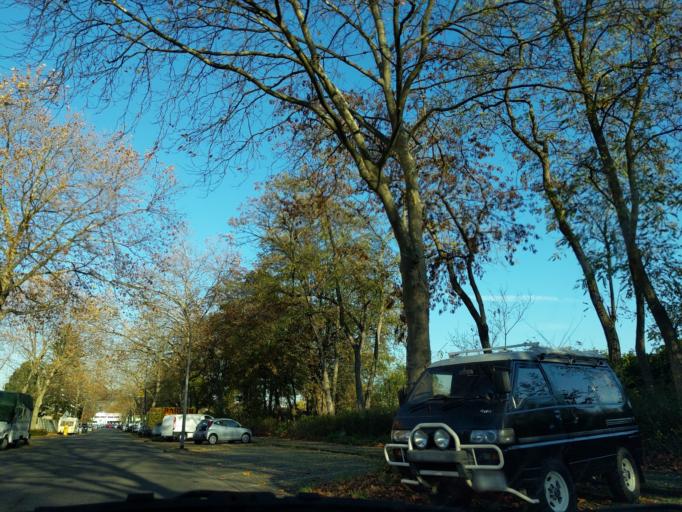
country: DE
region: North Rhine-Westphalia
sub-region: Regierungsbezirk Koln
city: Mengenich
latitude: 50.9726
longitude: 6.8950
